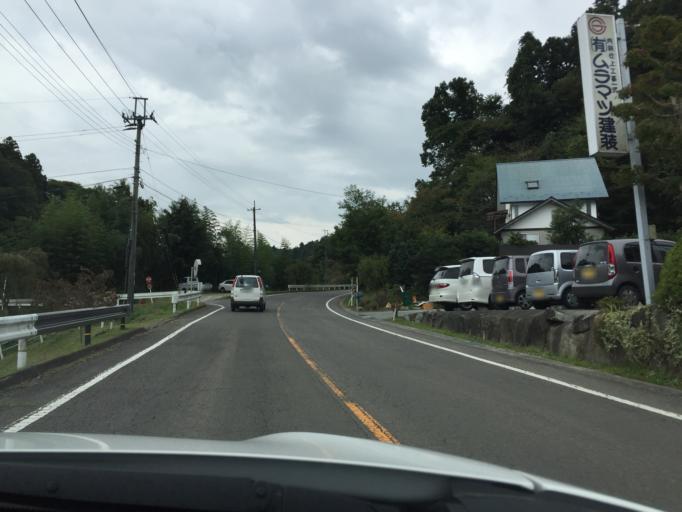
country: JP
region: Fukushima
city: Nihommatsu
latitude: 37.6140
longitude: 140.5372
